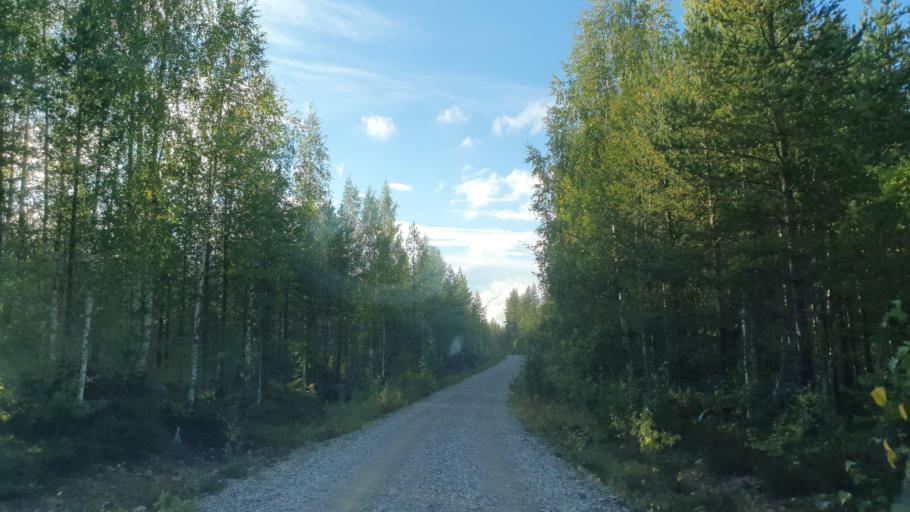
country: FI
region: Kainuu
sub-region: Kehys-Kainuu
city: Kuhmo
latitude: 64.3348
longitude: 29.9968
